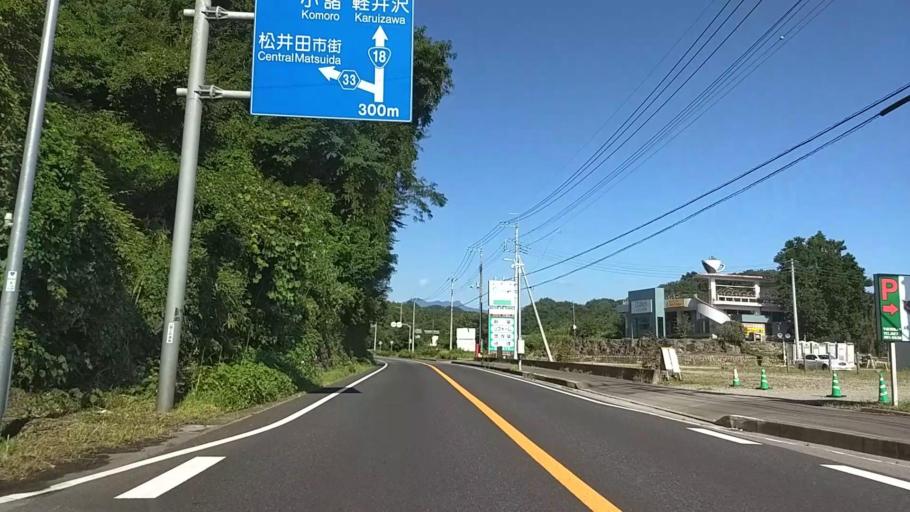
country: JP
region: Gunma
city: Annaka
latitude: 36.3071
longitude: 138.8216
